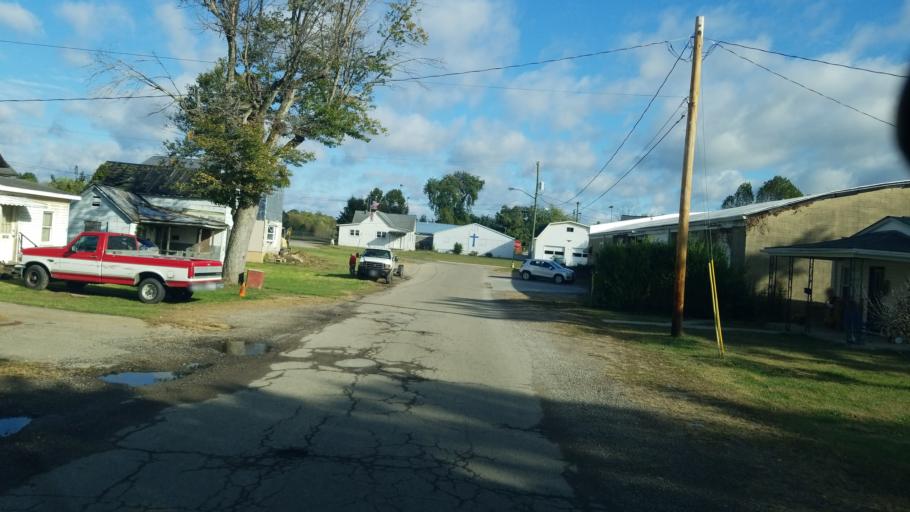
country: US
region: Ohio
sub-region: Jackson County
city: Wellston
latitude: 39.1139
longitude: -82.5359
